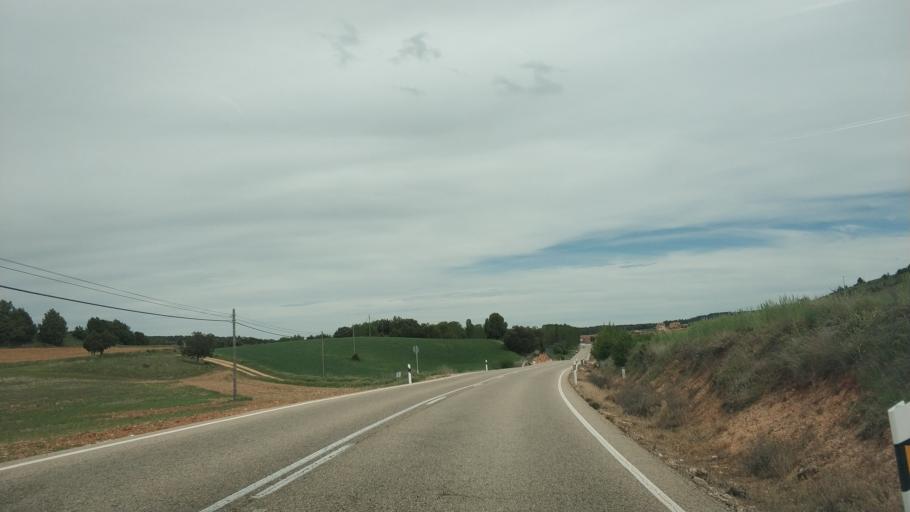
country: ES
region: Castille and Leon
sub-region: Provincia de Soria
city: El Burgo de Osma
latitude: 41.5743
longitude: -3.0197
